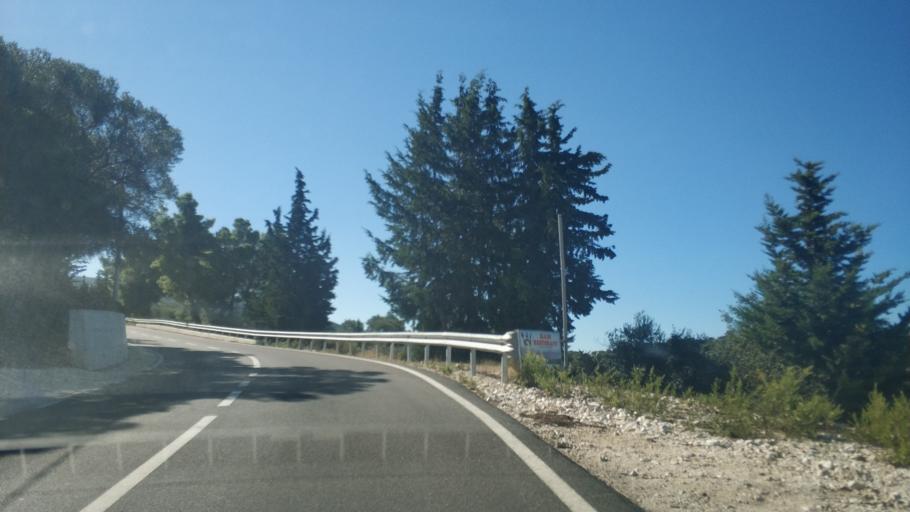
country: AL
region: Vlore
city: Vlore
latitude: 40.4536
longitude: 19.5151
